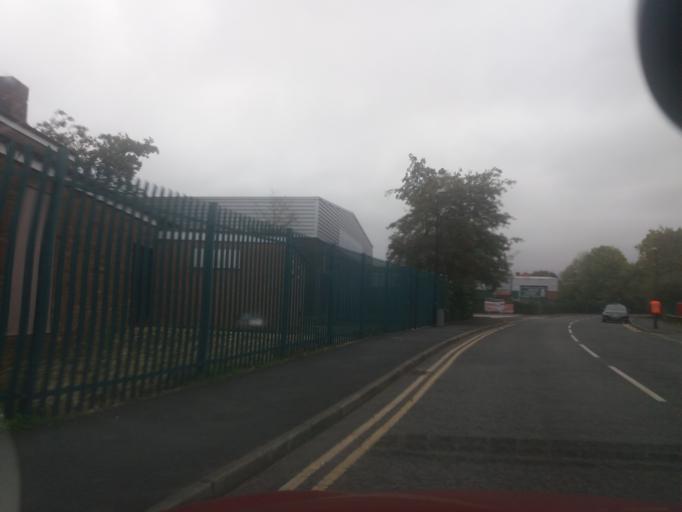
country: GB
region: England
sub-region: Lancashire
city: Chorley
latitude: 53.6535
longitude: -2.6258
